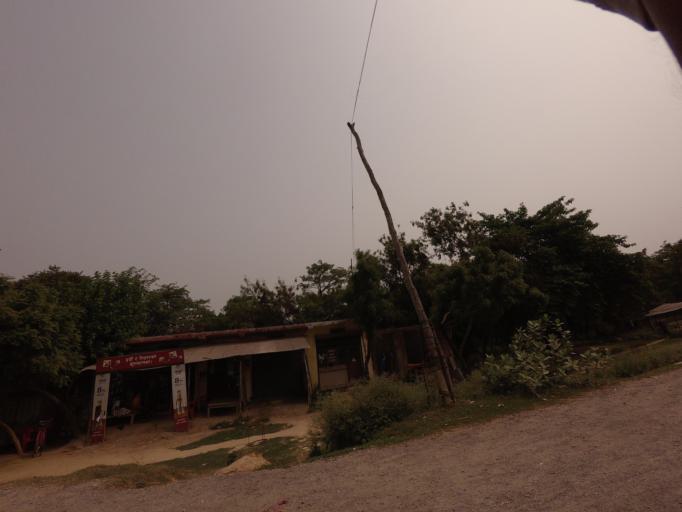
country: NP
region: Western Region
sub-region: Lumbini Zone
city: Bhairahawa
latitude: 27.5059
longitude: 83.3626
